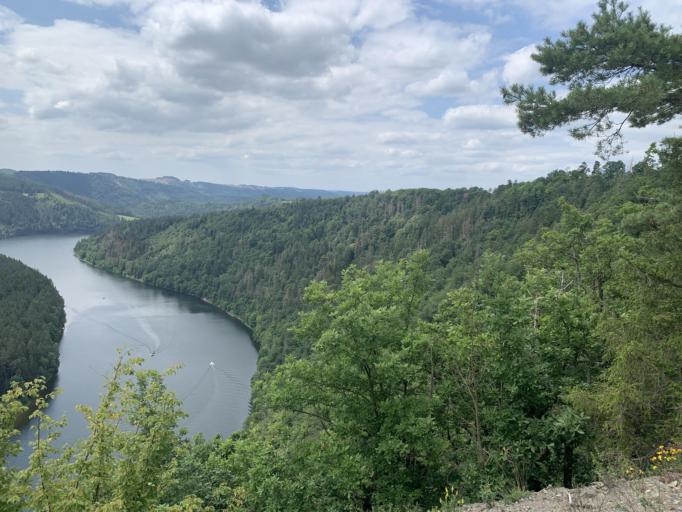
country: DE
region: Thuringia
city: Paska
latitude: 50.6138
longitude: 11.6338
